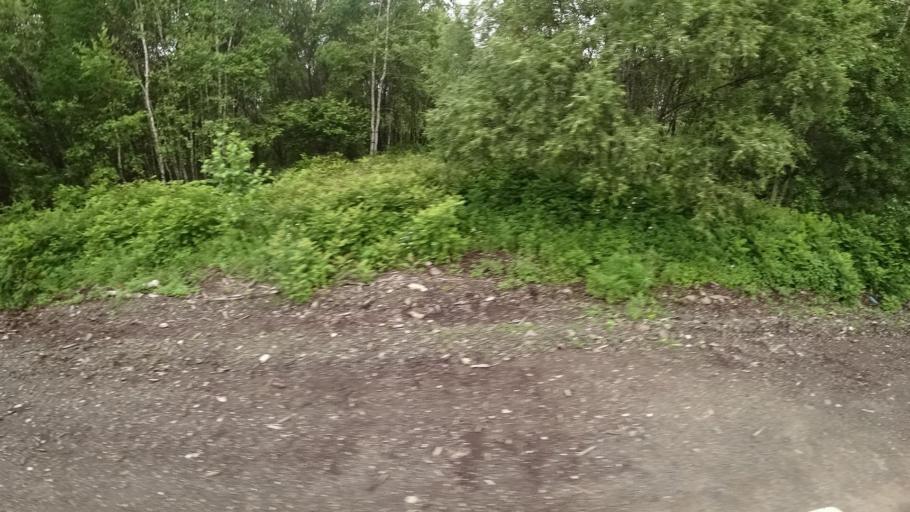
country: RU
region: Khabarovsk Krai
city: Amursk
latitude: 49.9123
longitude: 136.1581
